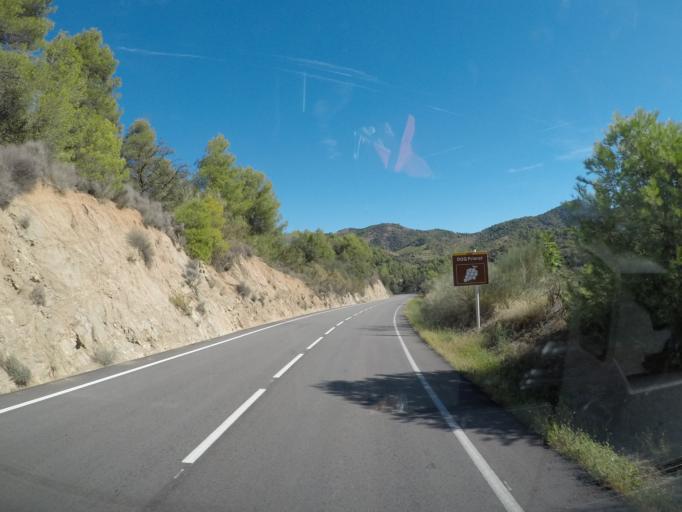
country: ES
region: Catalonia
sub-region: Provincia de Tarragona
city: Falset
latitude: 41.1650
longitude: 0.8186
